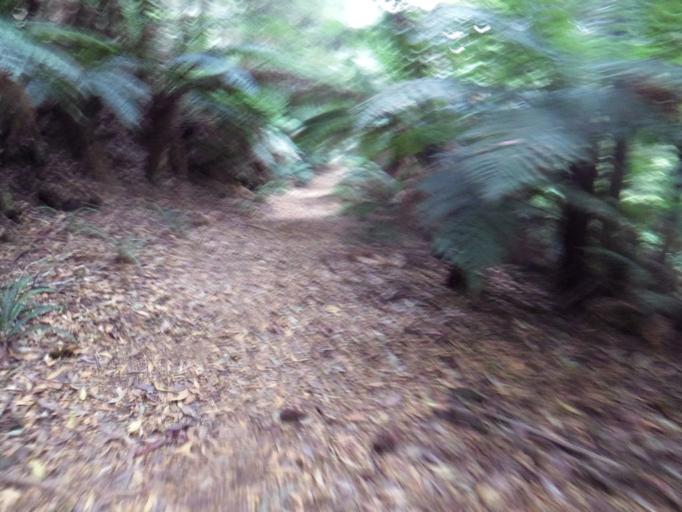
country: AU
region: Victoria
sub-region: Yarra Ranges
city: Healesville
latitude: -37.5165
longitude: 145.5204
